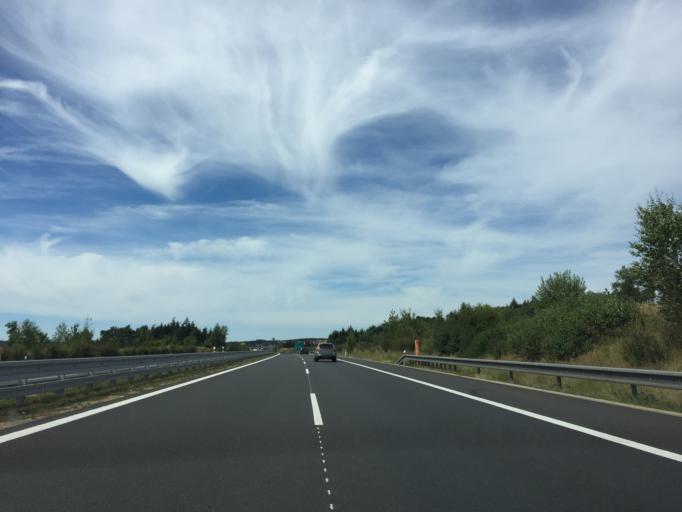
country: CZ
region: Jihocesky
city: Chotoviny
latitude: 49.4609
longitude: 14.6657
